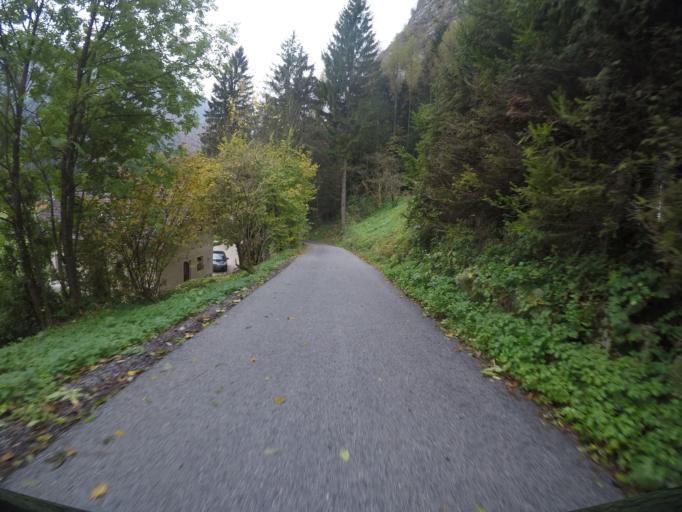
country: SI
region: Kranjska Gora
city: Mojstrana
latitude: 46.4595
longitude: 13.9345
